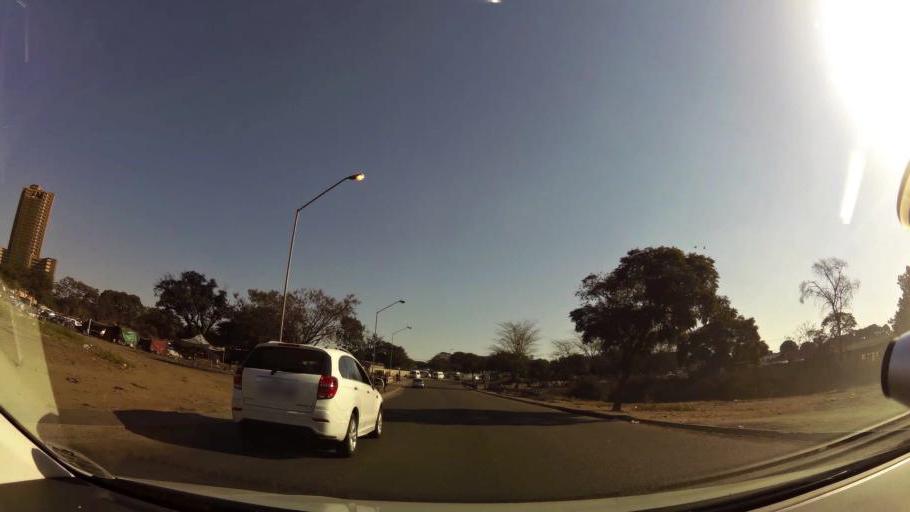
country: ZA
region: Gauteng
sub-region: City of Tshwane Metropolitan Municipality
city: Pretoria
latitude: -25.7413
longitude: 28.1794
